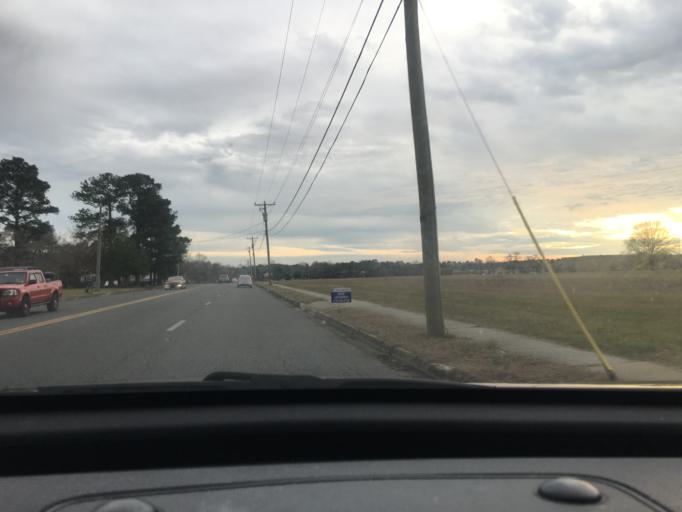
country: US
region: Maryland
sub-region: Wicomico County
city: Salisbury
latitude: 38.3652
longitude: -75.5672
